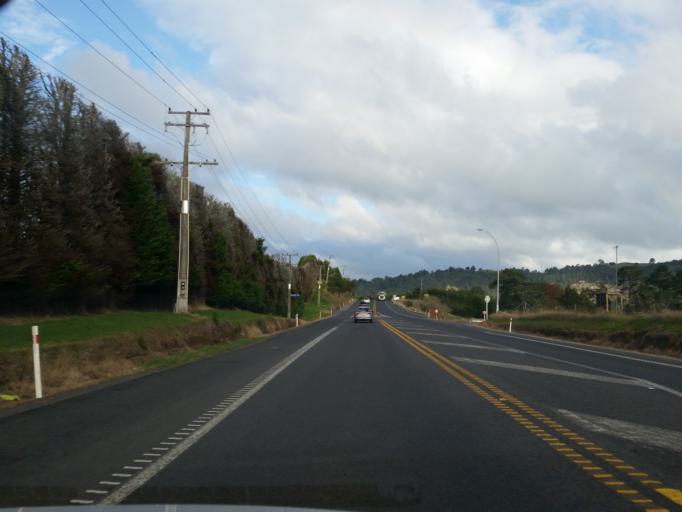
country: NZ
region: Bay of Plenty
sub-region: Tauranga City
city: Tauranga
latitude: -37.6871
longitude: 176.0389
